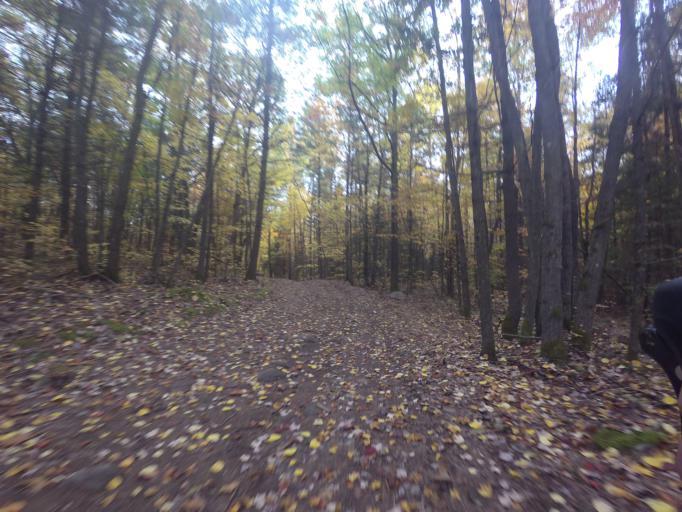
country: CA
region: Ontario
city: Petawawa
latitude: 45.7513
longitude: -77.3506
